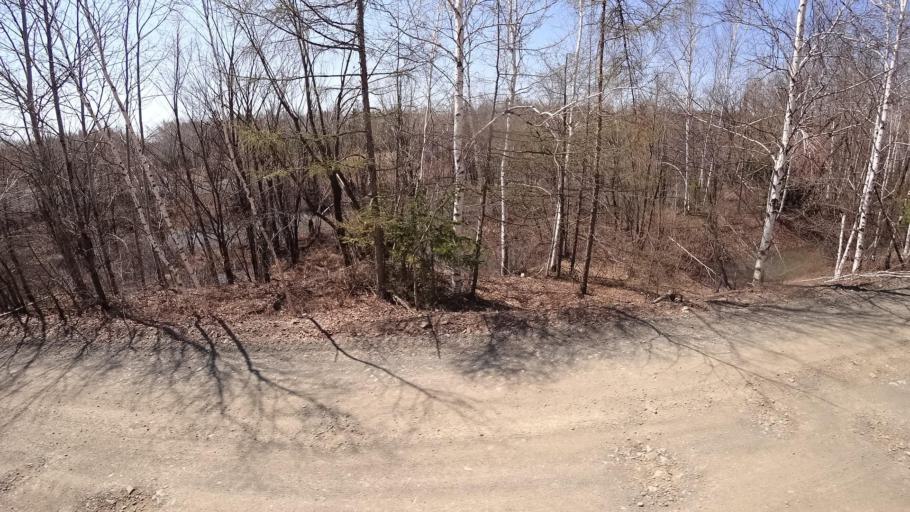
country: RU
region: Khabarovsk Krai
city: Khurba
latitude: 50.4123
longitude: 136.8429
